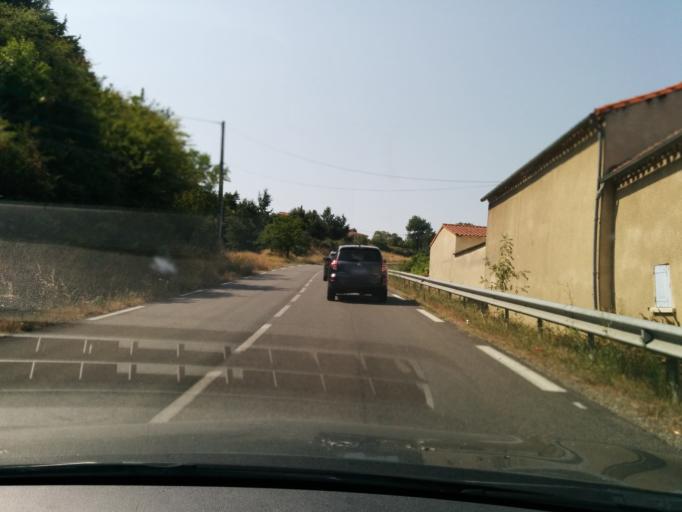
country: FR
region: Midi-Pyrenees
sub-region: Departement du Tarn
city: Castelnau-de-Levis
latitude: 43.9532
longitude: 2.1164
